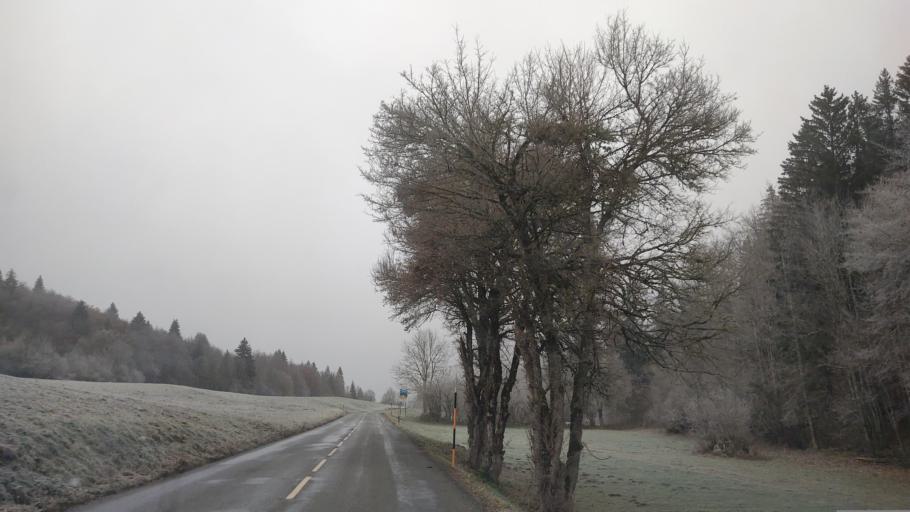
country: FR
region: Rhone-Alpes
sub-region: Departement de la Savoie
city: Coise-Saint-Jean-Pied-Gauthier
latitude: 45.5847
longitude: 6.1364
